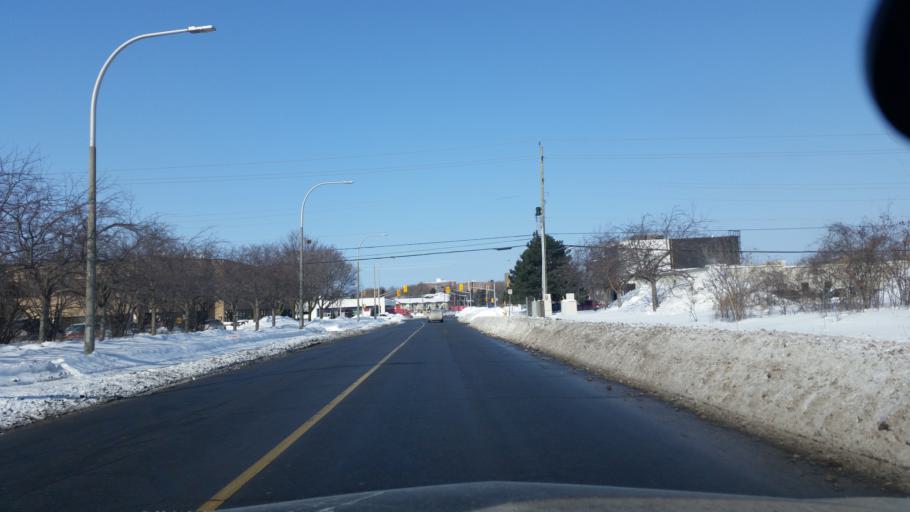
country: CA
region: Ontario
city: Ottawa
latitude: 45.3413
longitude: -75.7200
